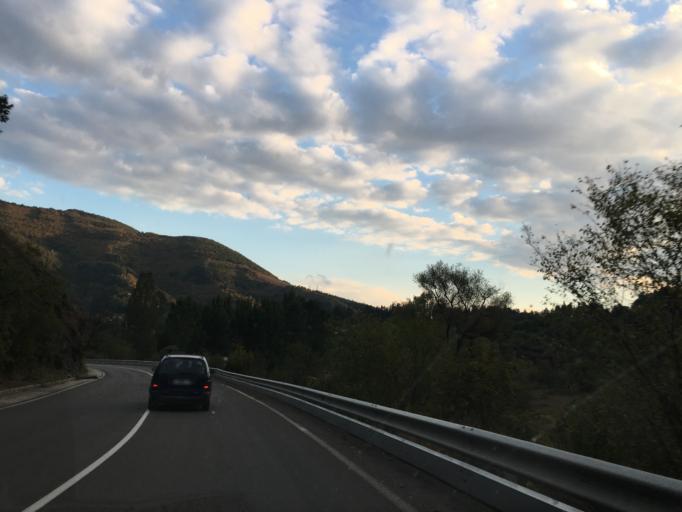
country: BG
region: Sofiya
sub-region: Obshtina Svoge
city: Svoge
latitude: 42.8877
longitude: 23.3876
